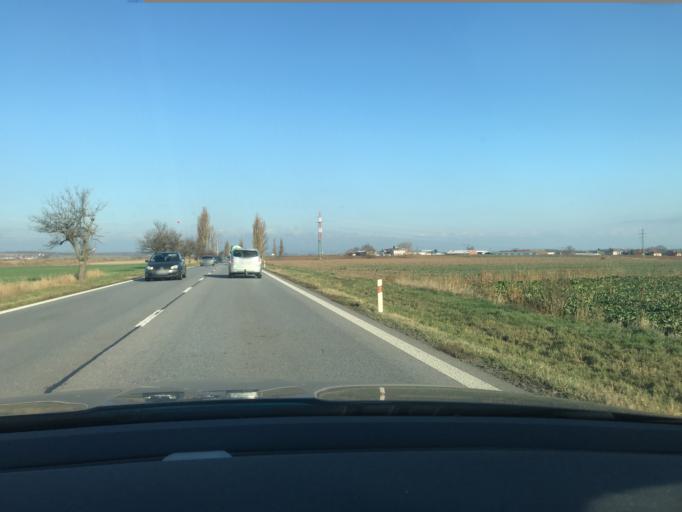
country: CZ
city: Predmerice nad Labem
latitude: 50.2580
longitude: 15.8052
